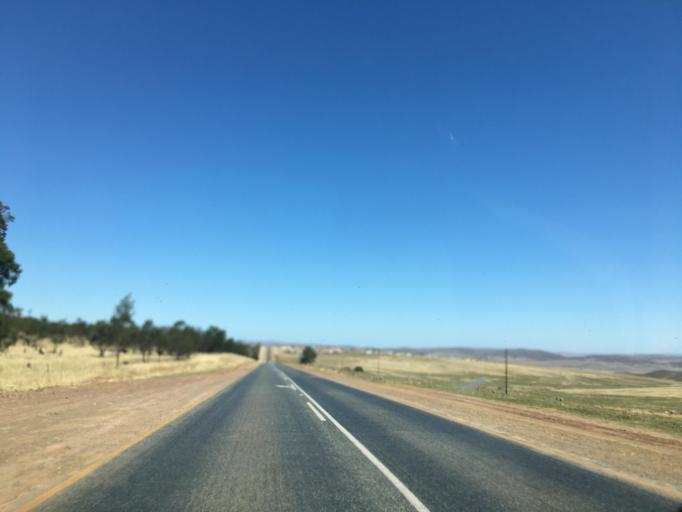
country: ZA
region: Eastern Cape
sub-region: Chris Hani District Municipality
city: Cofimvaba
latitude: -31.9136
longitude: 27.8383
